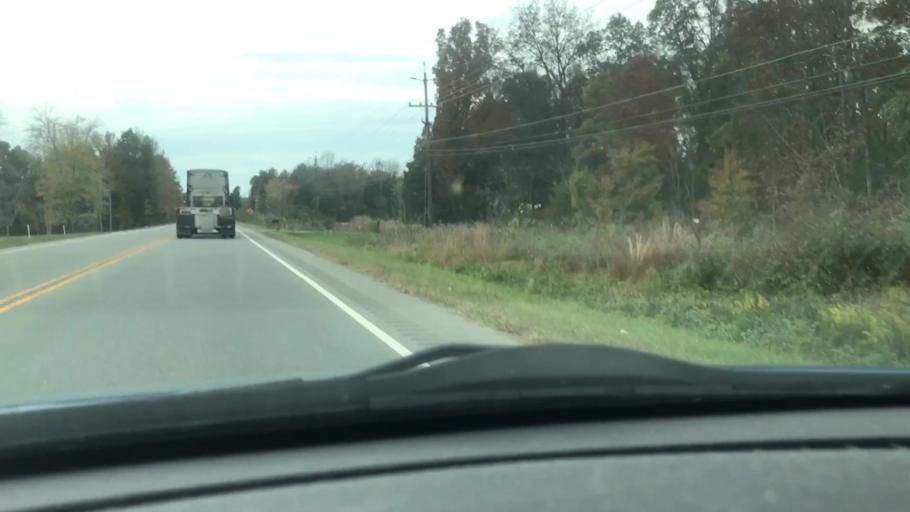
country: US
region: North Carolina
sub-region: Davidson County
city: Thomasville
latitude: 35.7756
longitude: -80.1132
